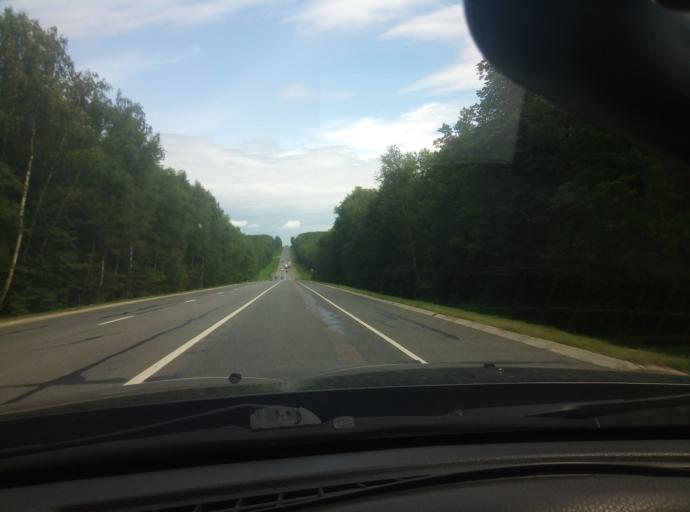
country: RU
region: Tula
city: Barsuki
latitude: 54.2717
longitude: 37.5347
